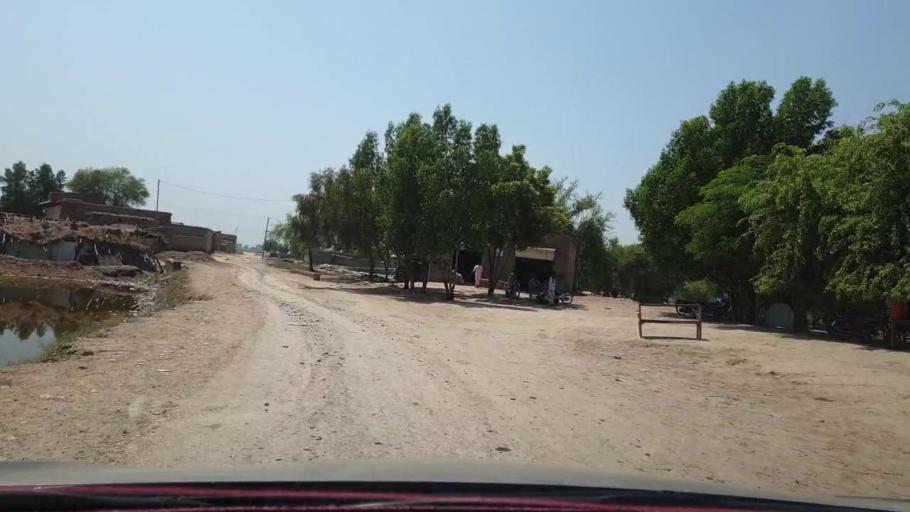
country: PK
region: Sindh
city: Warah
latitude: 27.5716
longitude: 67.8057
